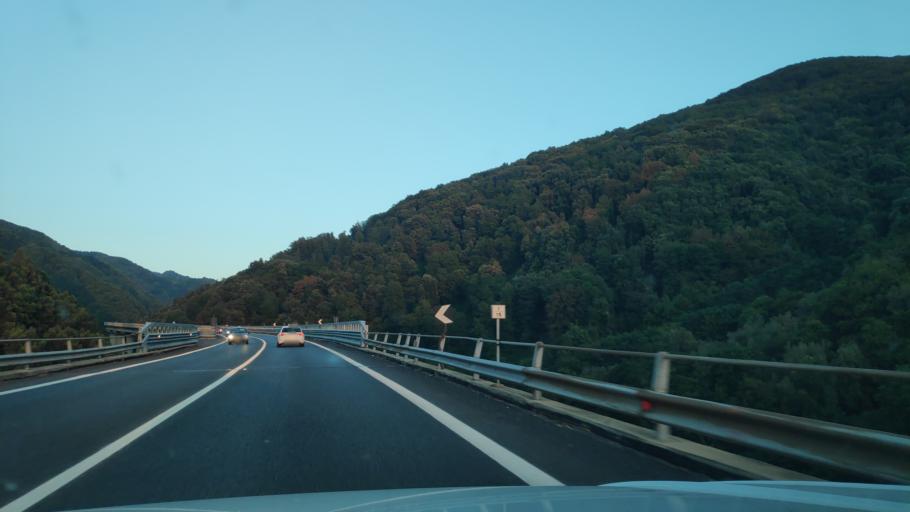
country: IT
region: Calabria
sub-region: Provincia di Reggio Calabria
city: Giffone
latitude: 38.4144
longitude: 16.1305
